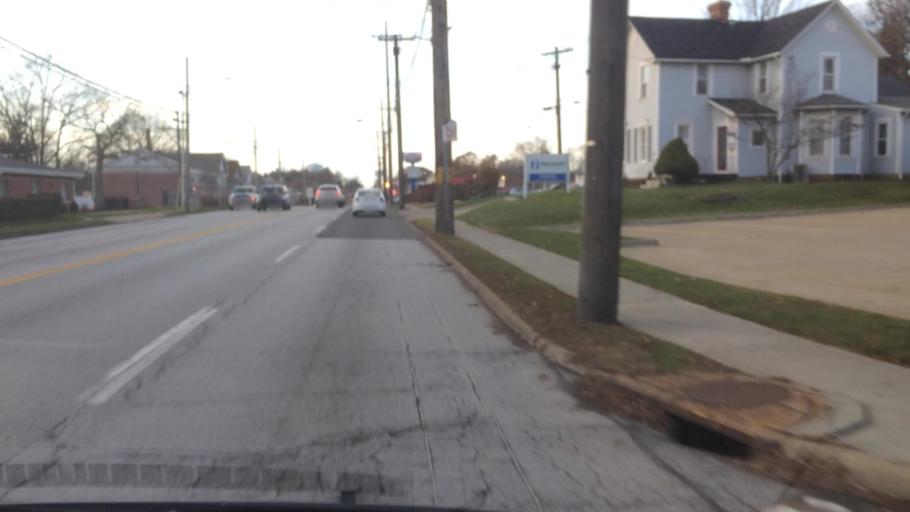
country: US
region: Ohio
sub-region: Summit County
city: Cuyahoga Falls
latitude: 41.1388
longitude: -81.4904
